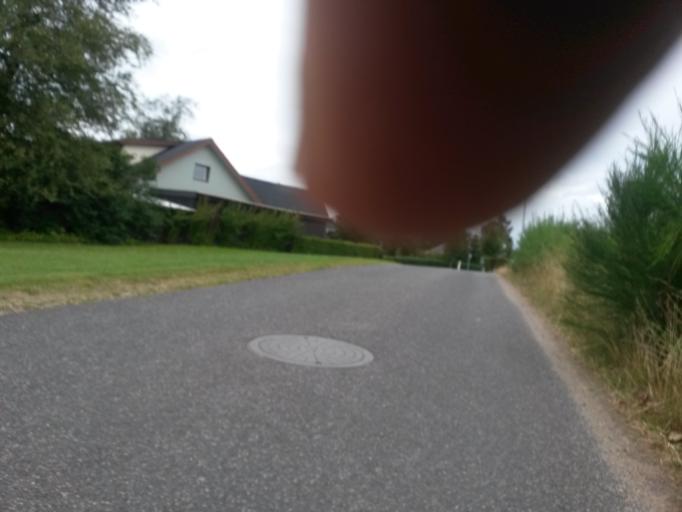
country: DK
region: Central Jutland
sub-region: Silkeborg Kommune
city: Kjellerup
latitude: 56.3229
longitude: 9.3373
